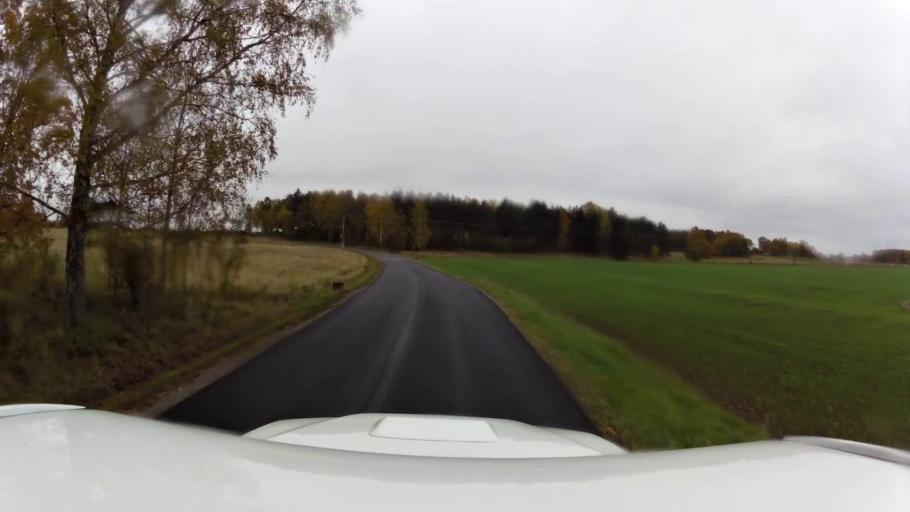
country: SE
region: OEstergoetland
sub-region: Linkopings Kommun
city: Ekangen
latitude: 58.4528
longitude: 15.7029
